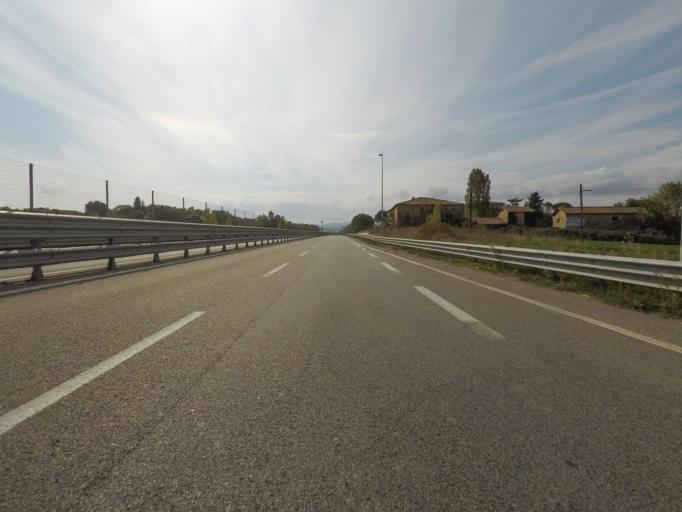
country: IT
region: Tuscany
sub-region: Provincia di Siena
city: Rosia
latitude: 43.2298
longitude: 11.2758
